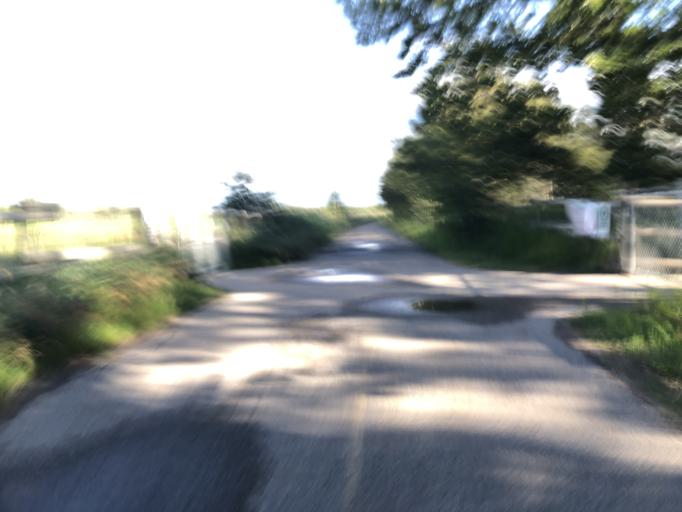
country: CA
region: Alberta
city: Calgary
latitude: 50.9623
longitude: -114.0259
